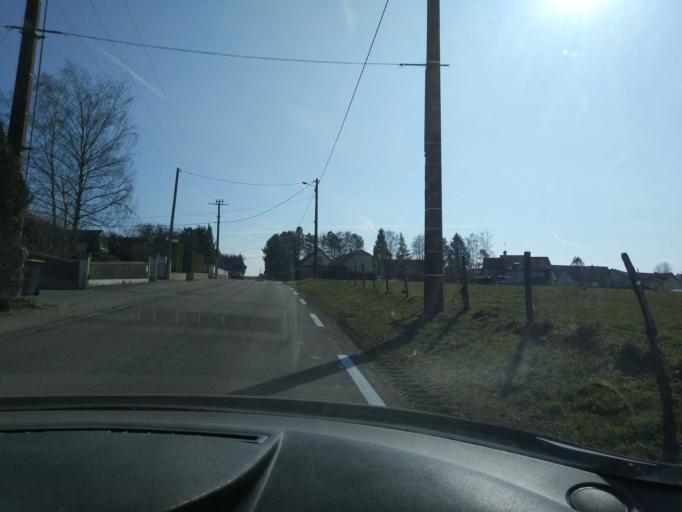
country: FR
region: Franche-Comte
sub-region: Departement du Doubs
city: Saone
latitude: 47.2208
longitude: 6.1235
